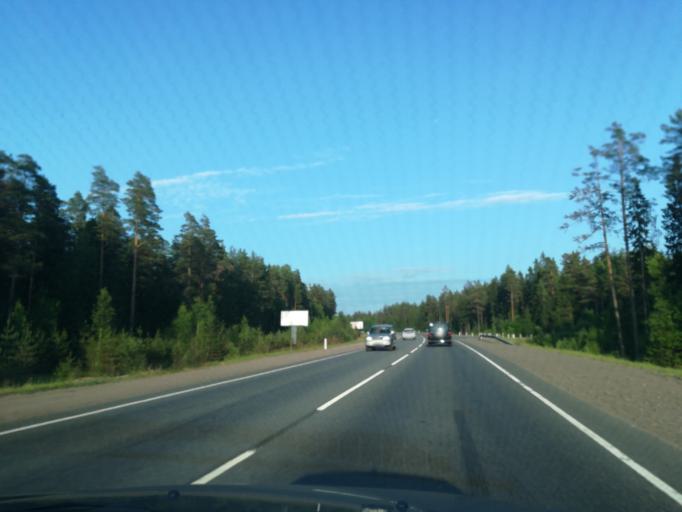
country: RU
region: Leningrad
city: Vyborg
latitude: 60.6700
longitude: 28.8861
